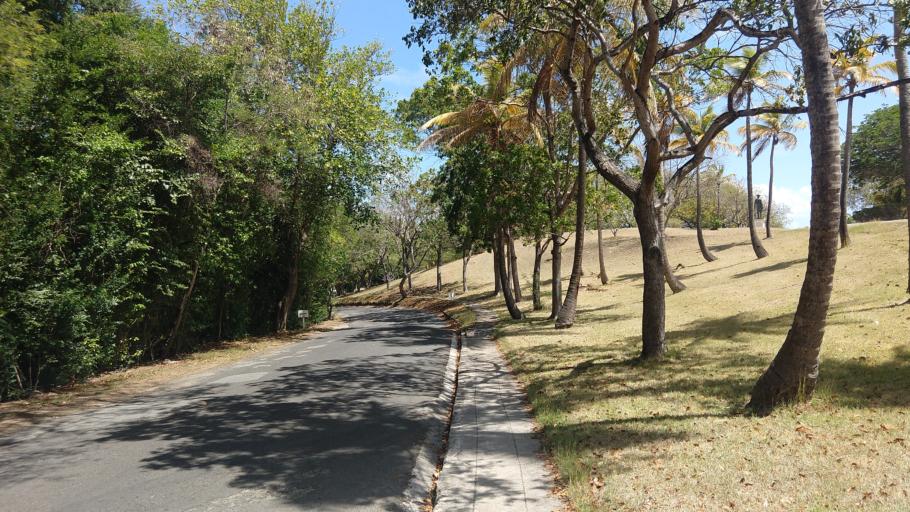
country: VC
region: Grenadines
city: Port Elizabeth
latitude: 12.8836
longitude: -61.1856
